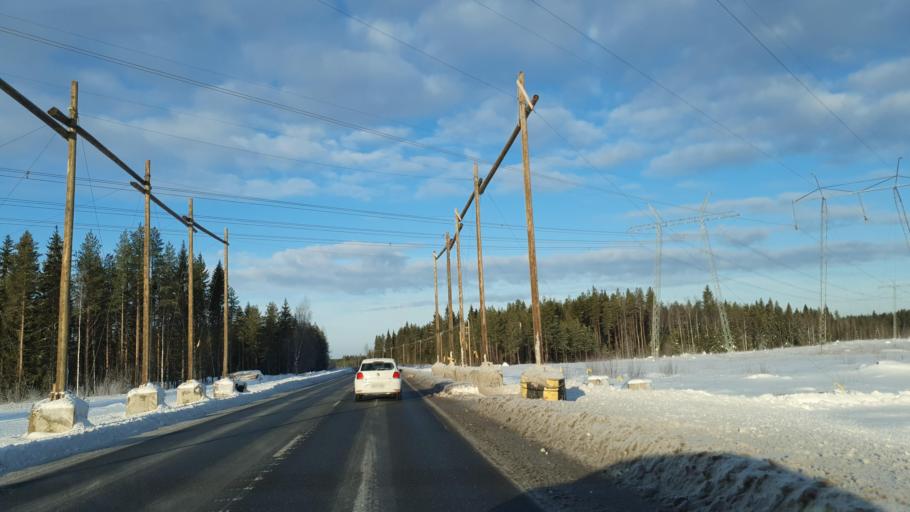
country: FI
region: Northern Ostrobothnia
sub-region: Oulu
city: Muhos
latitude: 64.7857
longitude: 26.1846
